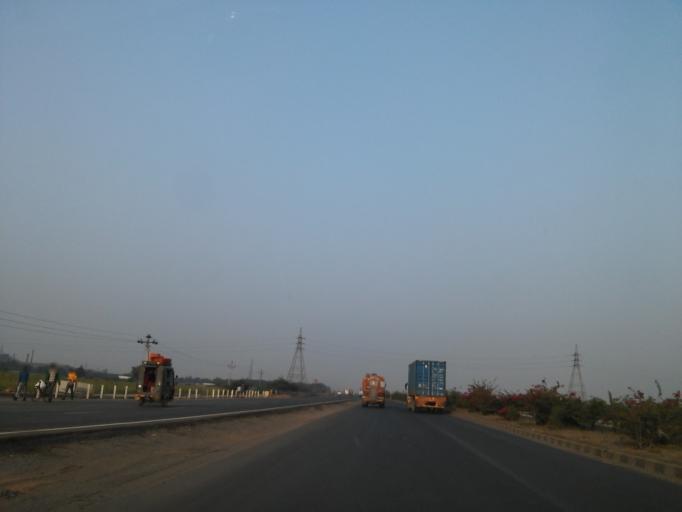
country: IN
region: Gujarat
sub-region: Kachchh
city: Bhachau
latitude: 23.3096
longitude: 70.4860
